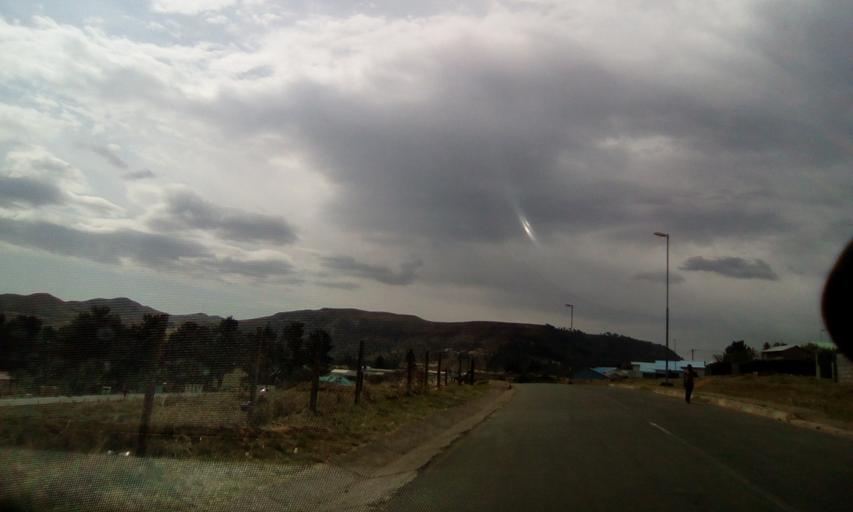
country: LS
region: Qacha's Nek
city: Qacha's Nek
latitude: -30.1134
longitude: 28.6759
